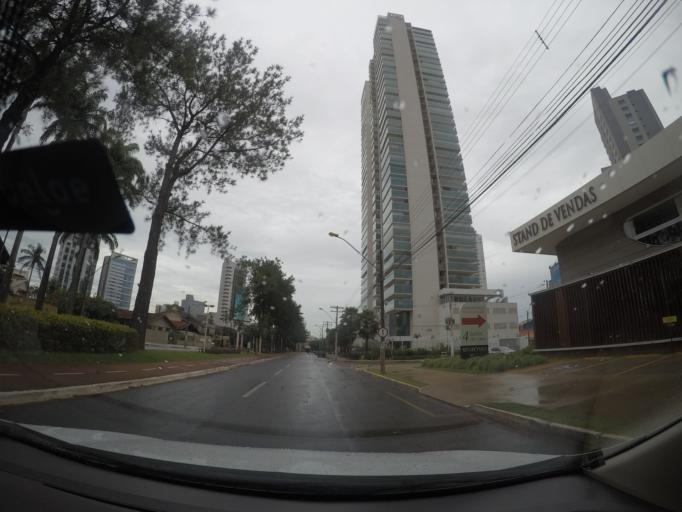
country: BR
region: Goias
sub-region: Goiania
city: Goiania
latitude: -16.6999
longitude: -49.2557
